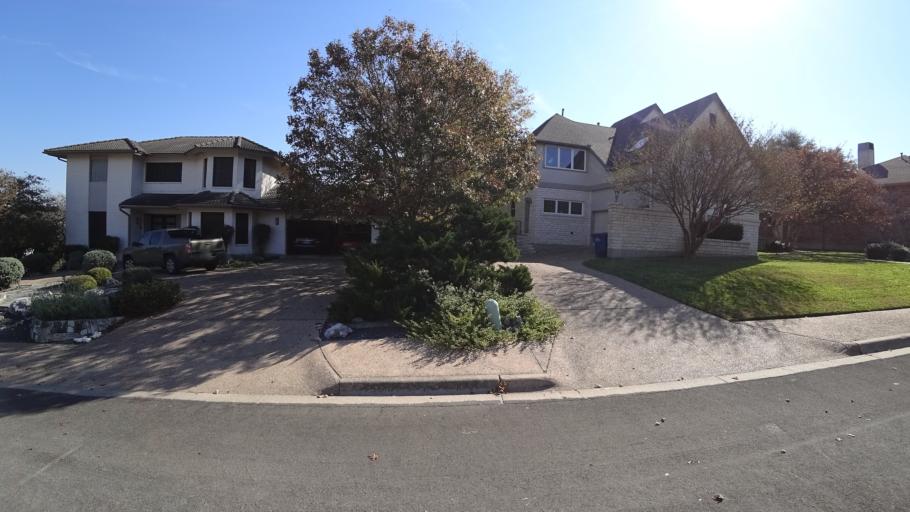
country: US
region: Texas
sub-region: Williamson County
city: Jollyville
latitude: 30.3741
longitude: -97.7700
